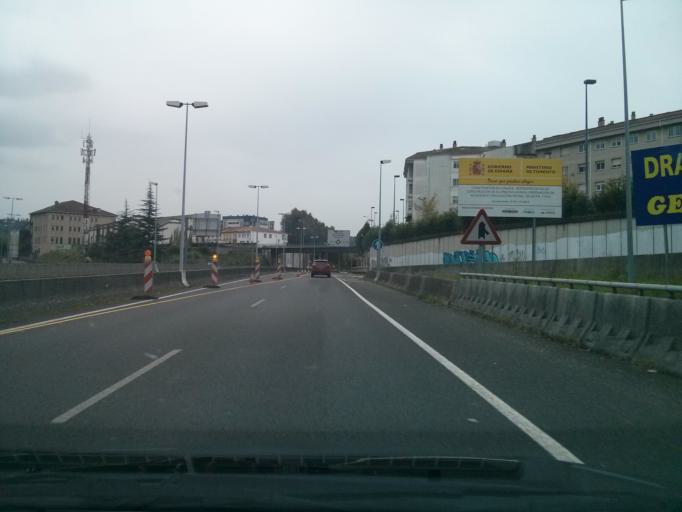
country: ES
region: Galicia
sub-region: Provincia da Coruna
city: Santiago de Compostela
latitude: 42.8674
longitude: -8.5528
